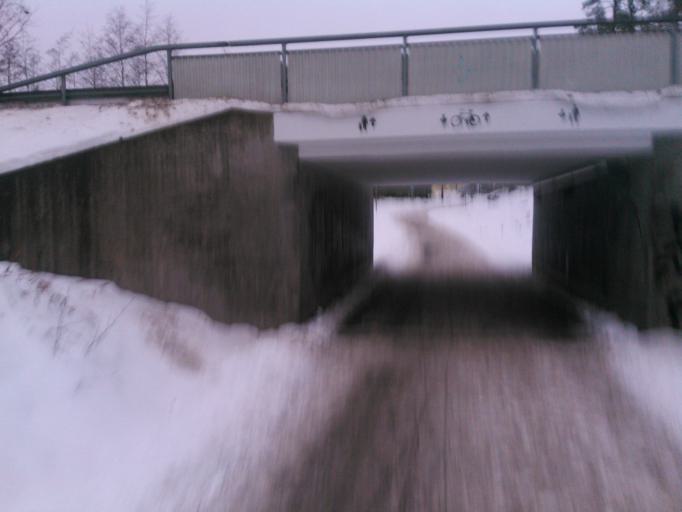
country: SE
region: Vaesterbotten
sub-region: Umea Kommun
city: Umea
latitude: 63.8141
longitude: 20.3125
